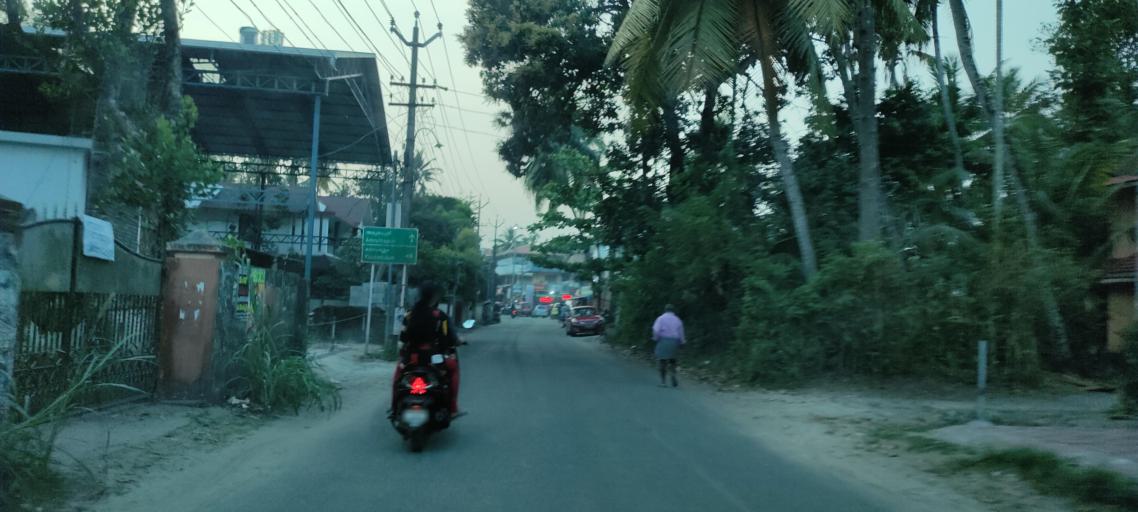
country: IN
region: Kerala
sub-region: Alappuzha
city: Kayankulam
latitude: 9.1205
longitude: 76.4909
